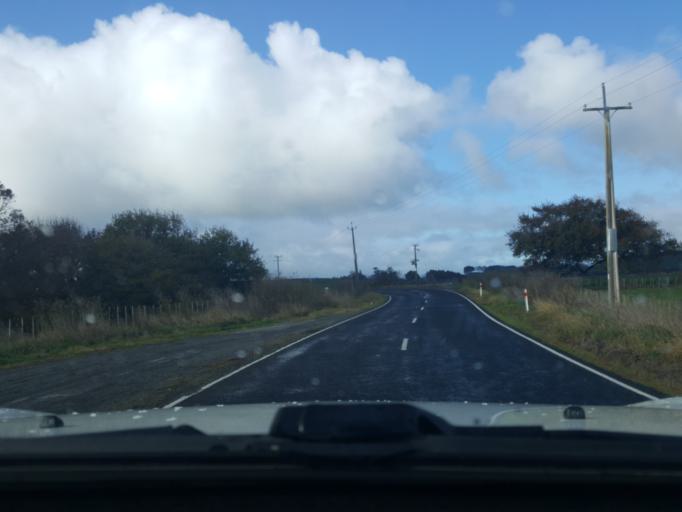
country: NZ
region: Waikato
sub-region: Waikato District
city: Te Kauwhata
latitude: -37.4483
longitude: 175.0943
